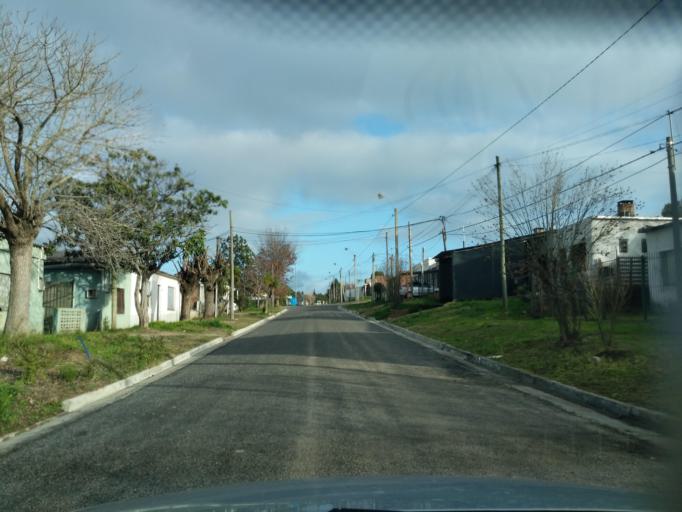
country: UY
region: Florida
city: Florida
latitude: -34.0849
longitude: -56.2107
